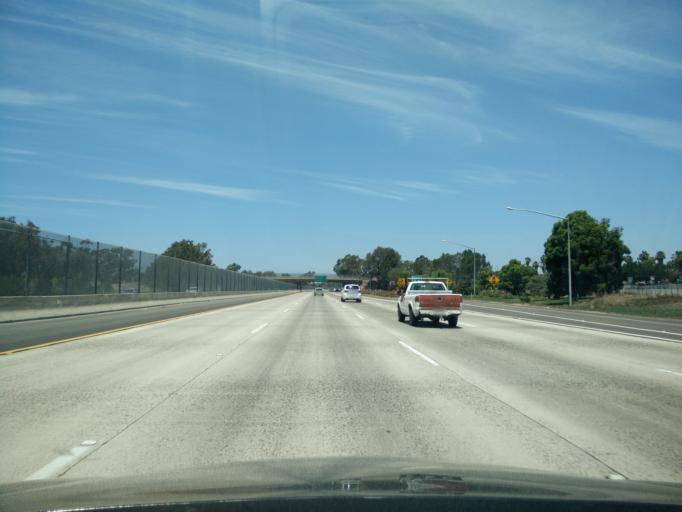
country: US
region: California
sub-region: San Diego County
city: Imperial Beach
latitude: 32.5574
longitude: -117.0592
